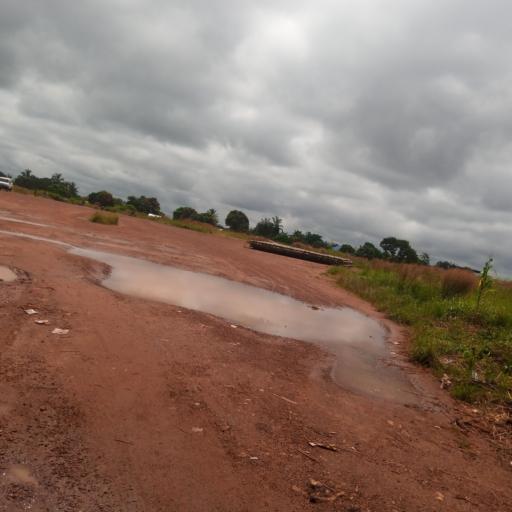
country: SL
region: Eastern Province
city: Kenema
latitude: 7.8975
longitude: -11.1751
